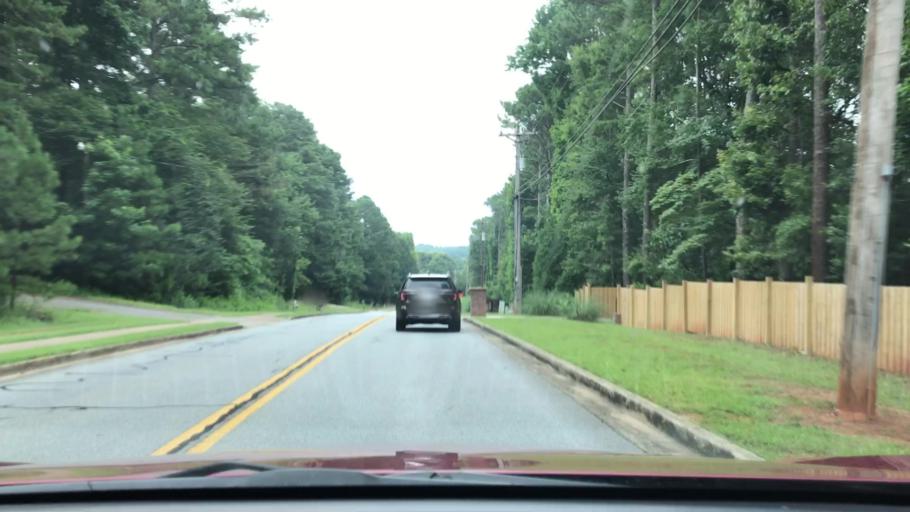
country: US
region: Georgia
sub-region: Gwinnett County
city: Suwanee
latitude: 34.0061
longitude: -84.0337
